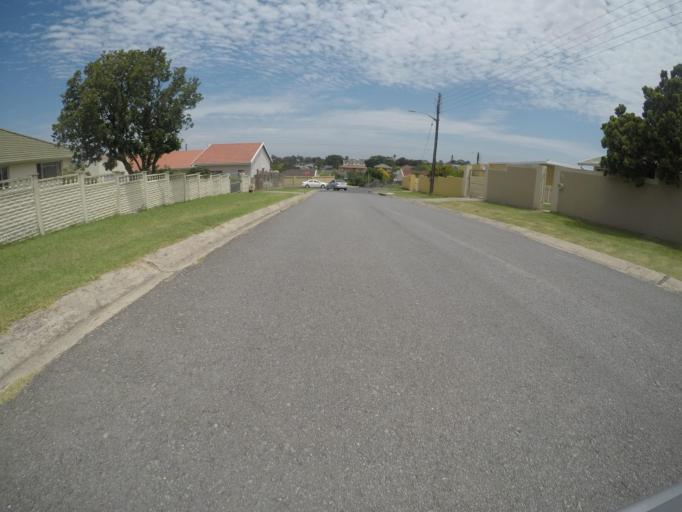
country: ZA
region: Eastern Cape
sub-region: Buffalo City Metropolitan Municipality
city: East London
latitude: -32.9850
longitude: 27.8657
